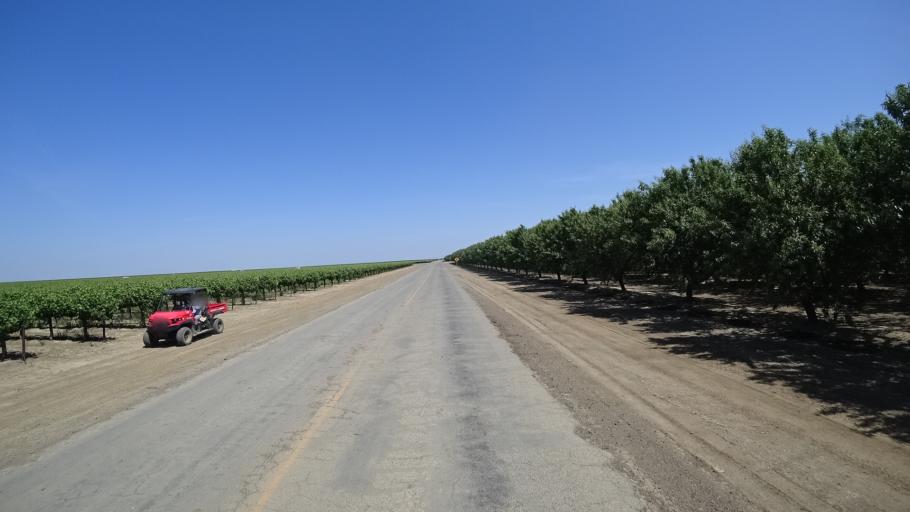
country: US
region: California
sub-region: Fresno County
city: Huron
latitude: 36.1414
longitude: -120.0040
